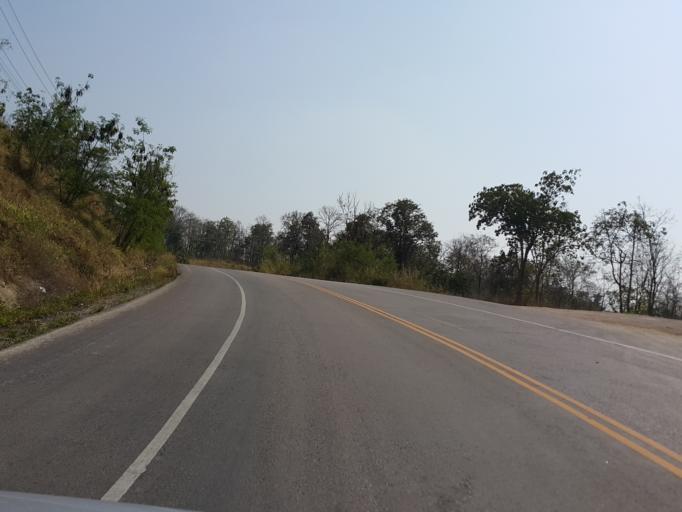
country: TH
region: Lampang
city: Mueang Pan
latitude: 18.8784
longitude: 99.6010
